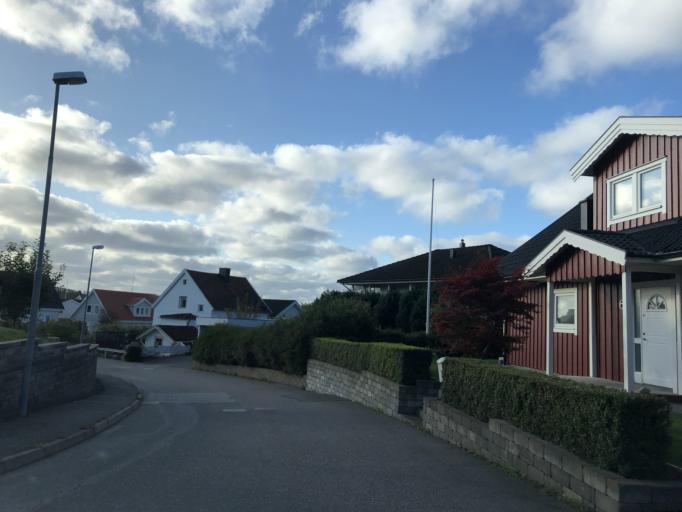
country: SE
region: Vaestra Goetaland
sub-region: Goteborg
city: Majorna
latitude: 57.6401
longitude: 11.8734
